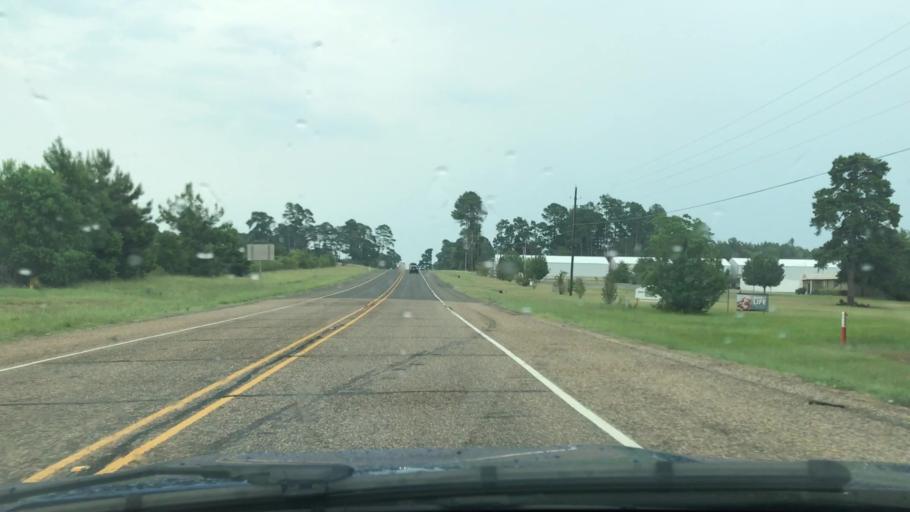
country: US
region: Texas
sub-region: Harrison County
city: Waskom
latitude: 32.4789
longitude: -94.0813
